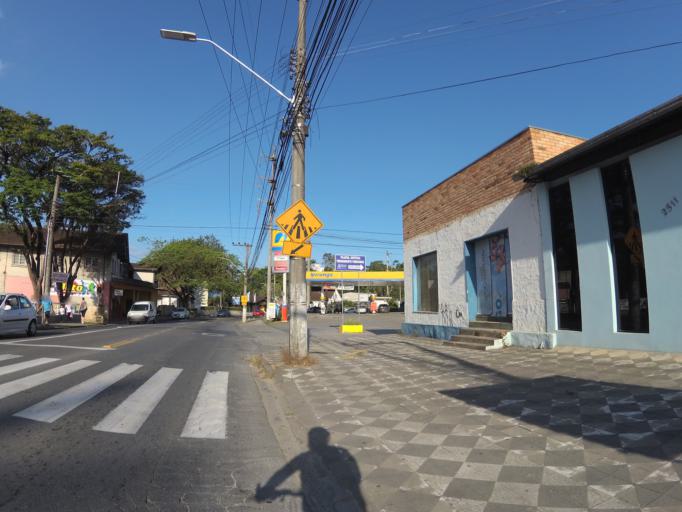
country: BR
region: Santa Catarina
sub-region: Blumenau
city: Blumenau
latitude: -26.9199
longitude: -49.0973
